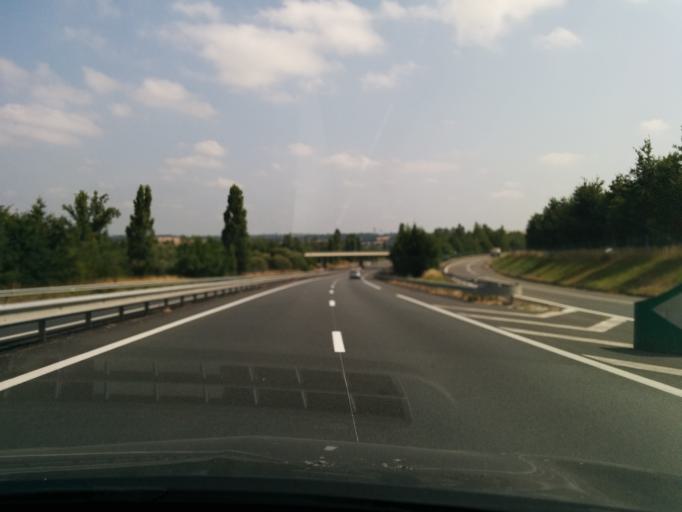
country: FR
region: Midi-Pyrenees
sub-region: Departement de la Haute-Garonne
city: Gragnague
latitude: 43.6845
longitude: 1.5626
